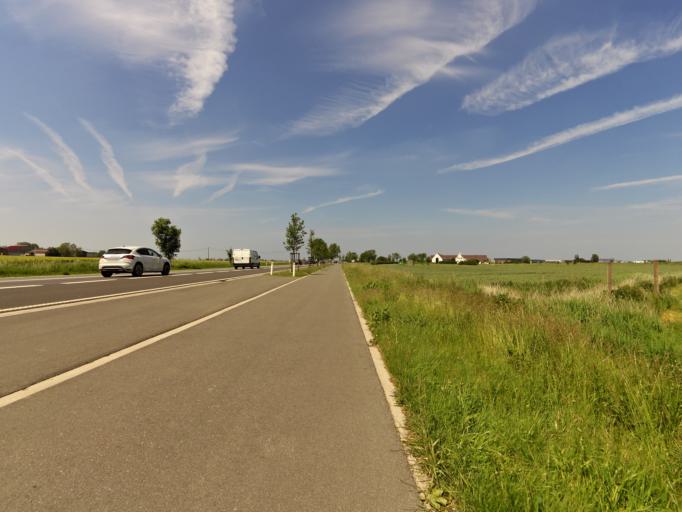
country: BE
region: Flanders
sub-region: Provincie West-Vlaanderen
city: Ostend
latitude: 51.1811
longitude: 2.9026
